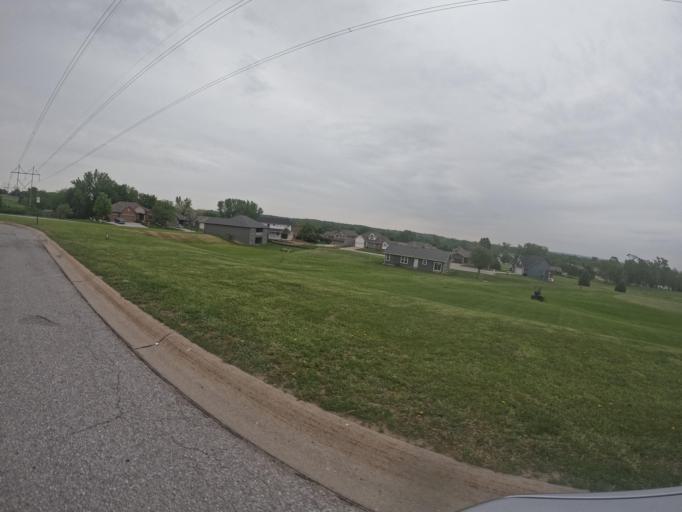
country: US
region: Nebraska
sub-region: Sarpy County
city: Offutt Air Force Base
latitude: 41.0463
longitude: -95.9592
